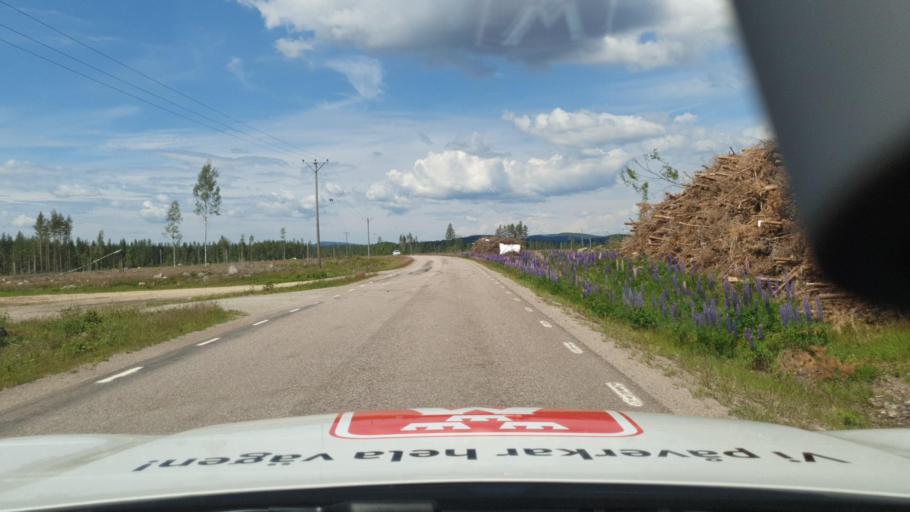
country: SE
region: Vaermland
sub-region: Torsby Kommun
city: Torsby
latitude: 60.5036
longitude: 12.8533
